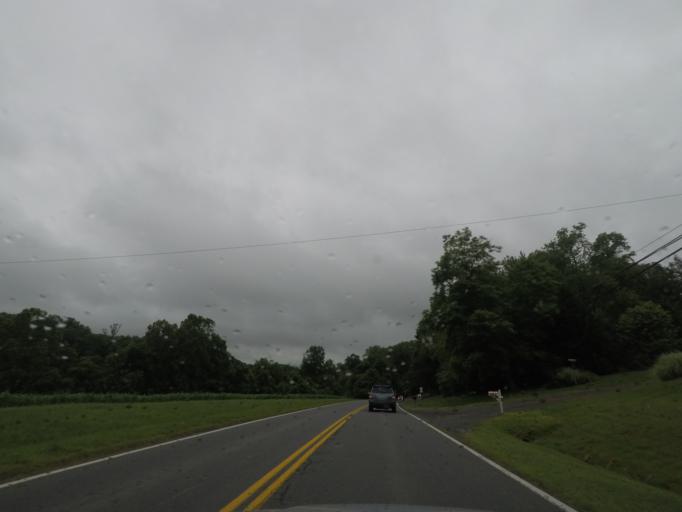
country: US
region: Virginia
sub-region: Orange County
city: Orange
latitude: 38.2659
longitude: -78.1222
